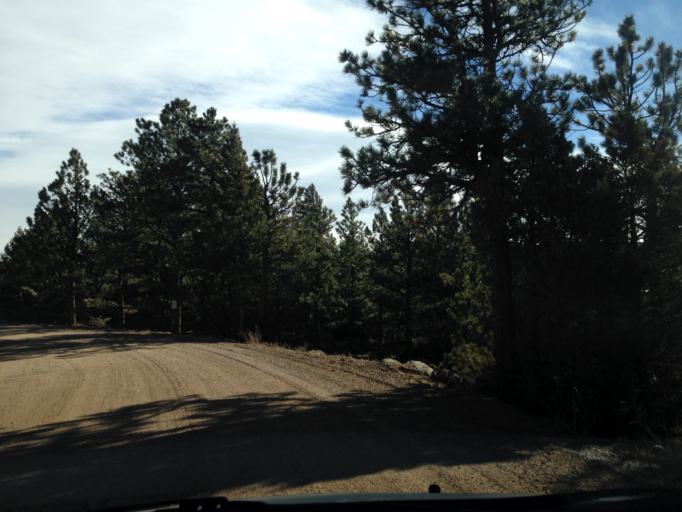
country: US
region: Colorado
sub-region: Boulder County
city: Coal Creek
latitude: 39.9435
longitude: -105.3500
